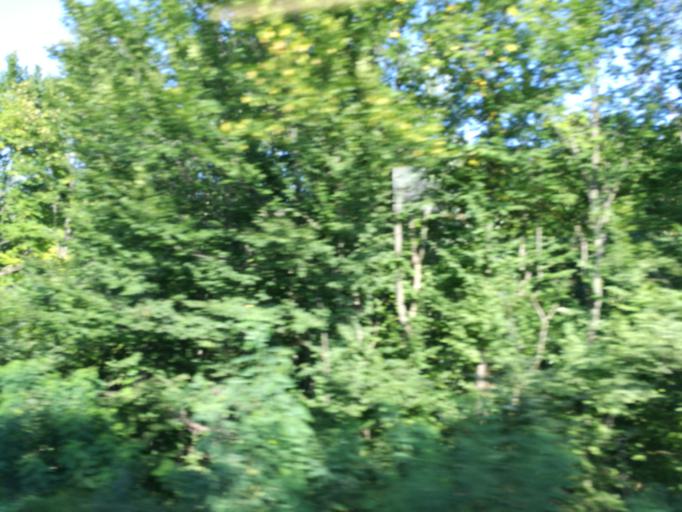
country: RO
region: Iasi
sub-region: Comuna Ciurea
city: Ciurea
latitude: 47.0220
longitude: 27.5819
